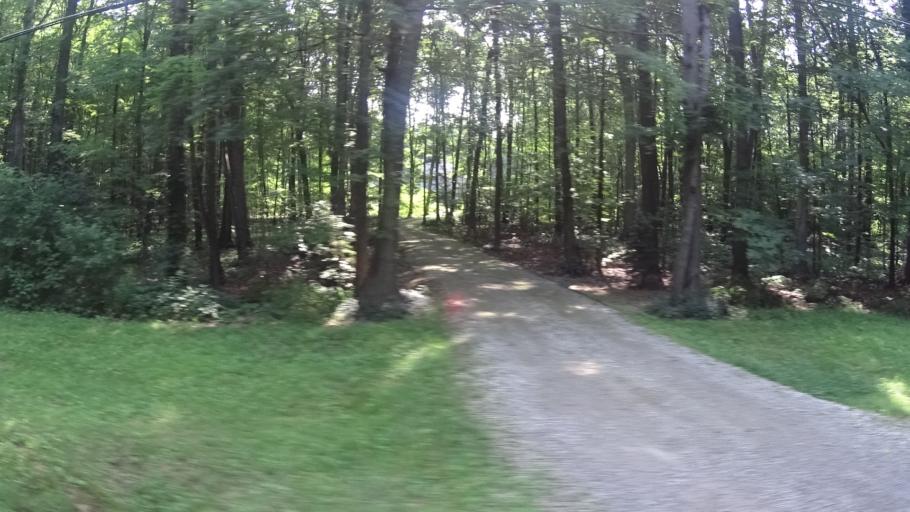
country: US
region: Ohio
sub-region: Lorain County
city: Vermilion
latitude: 41.3722
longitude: -82.4306
